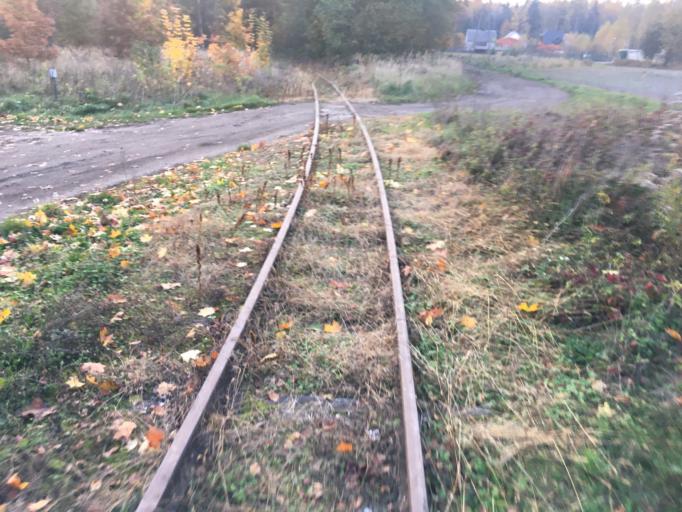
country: PL
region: Swietokrzyskie
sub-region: Powiat starachowicki
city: Starachowice
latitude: 51.0675
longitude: 21.1277
